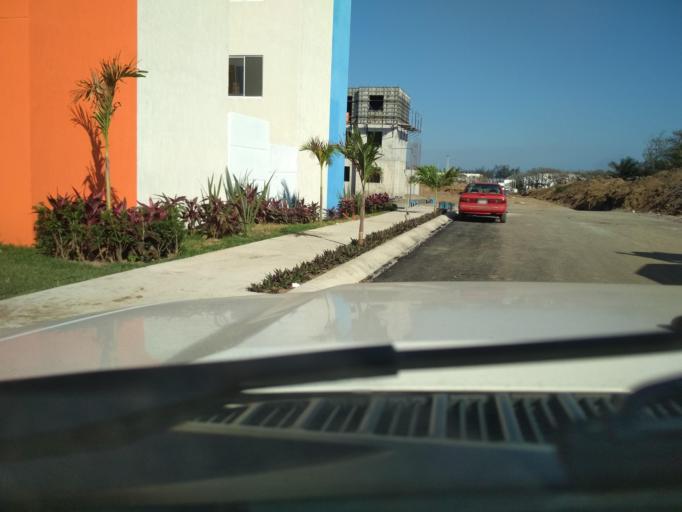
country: MX
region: Veracruz
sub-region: Veracruz
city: Las Amapolas
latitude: 19.1437
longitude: -96.2332
